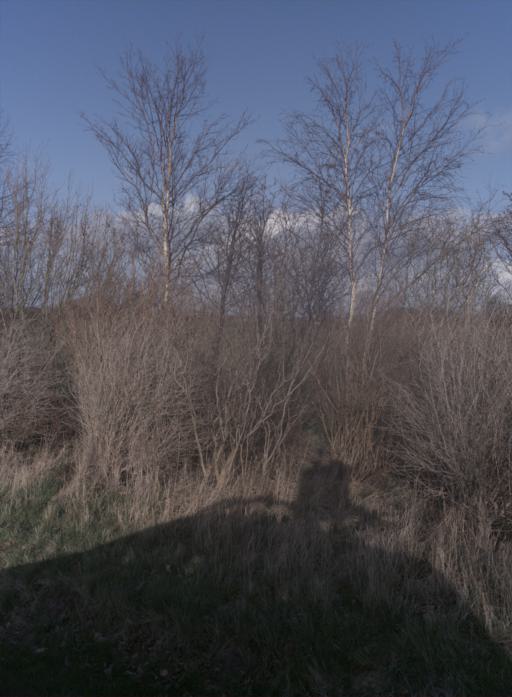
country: DK
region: Zealand
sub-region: Kalundborg Kommune
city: Kalundborg
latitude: 55.6918
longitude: 11.1365
